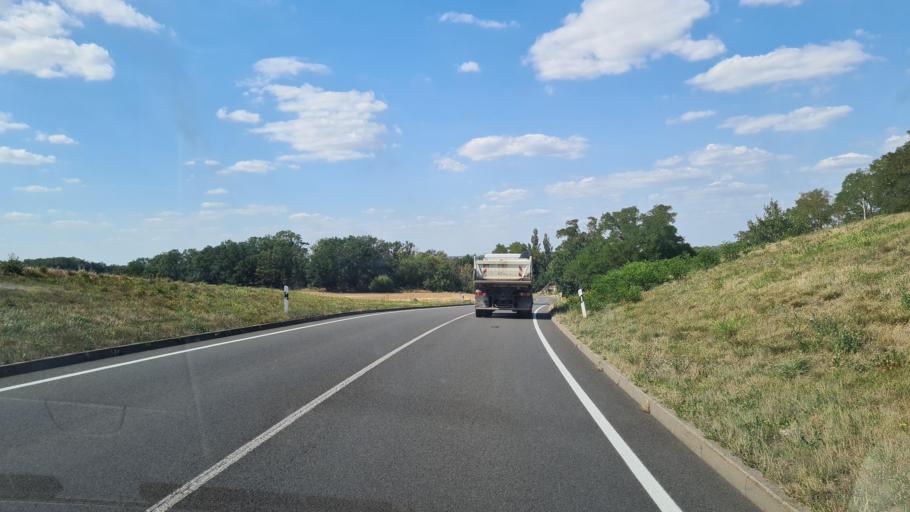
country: DE
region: Saxony
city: Eilenburg
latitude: 51.4306
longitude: 12.6259
